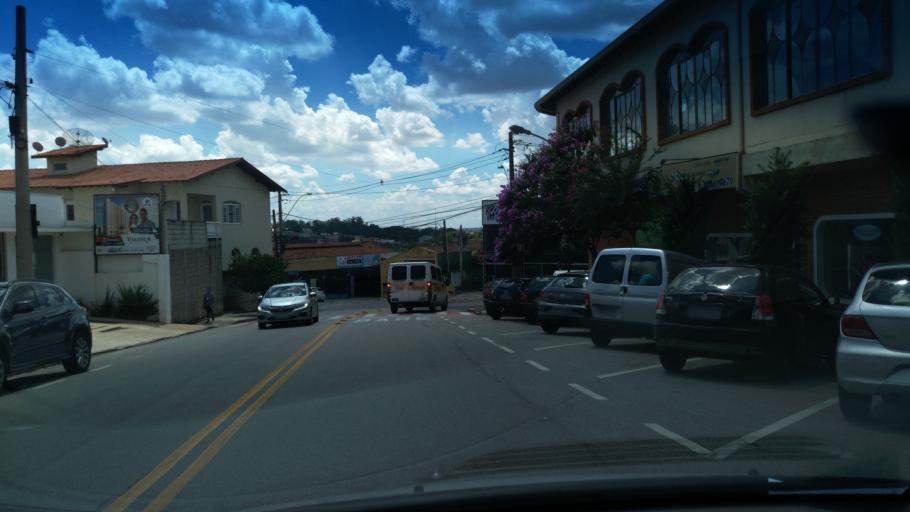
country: BR
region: Sao Paulo
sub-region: Vinhedo
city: Vinhedo
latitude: -23.0284
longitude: -46.9758
